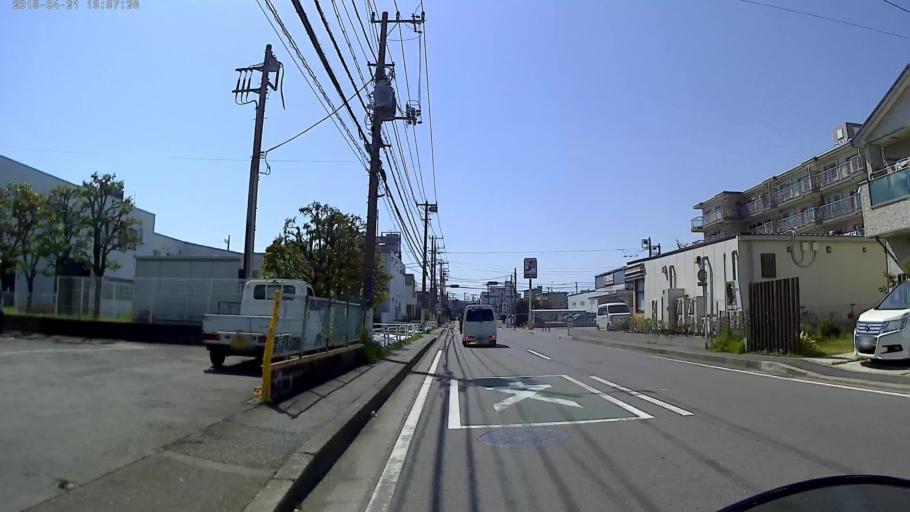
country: JP
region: Kanagawa
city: Hiratsuka
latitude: 35.3457
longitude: 139.3584
